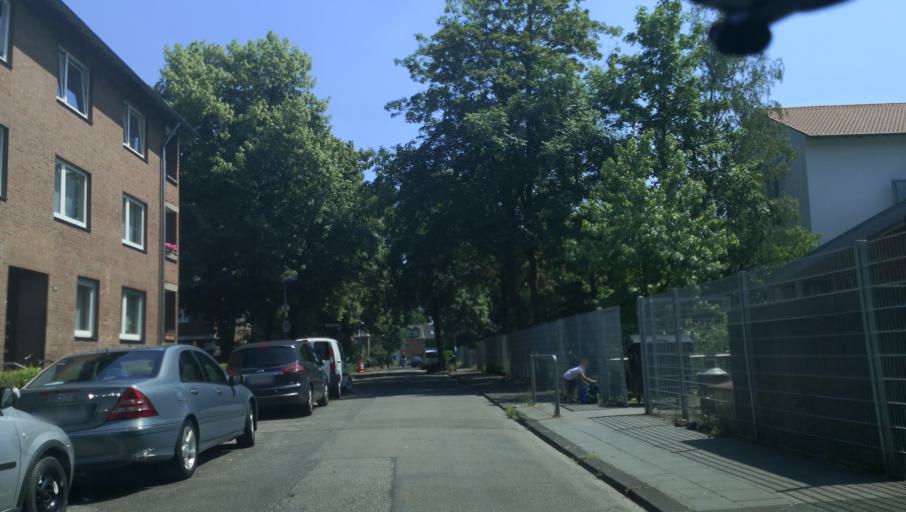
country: DE
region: North Rhine-Westphalia
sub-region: Regierungsbezirk Koln
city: Mengenich
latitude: 50.9654
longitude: 6.8942
